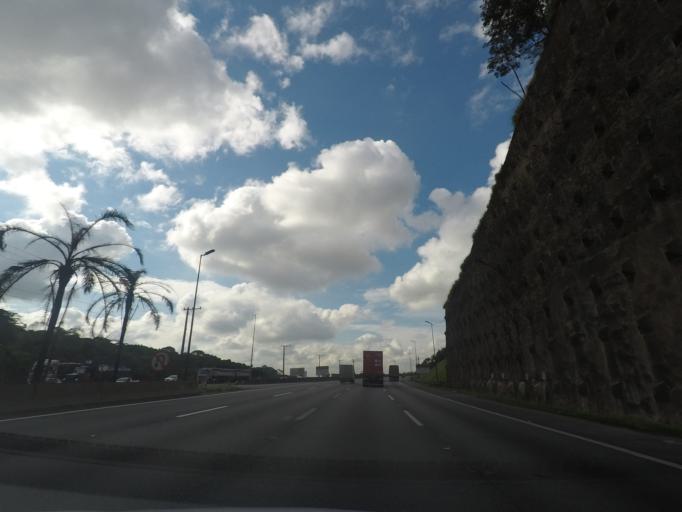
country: BR
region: Sao Paulo
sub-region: Embu
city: Embu
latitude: -23.6206
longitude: -46.8287
